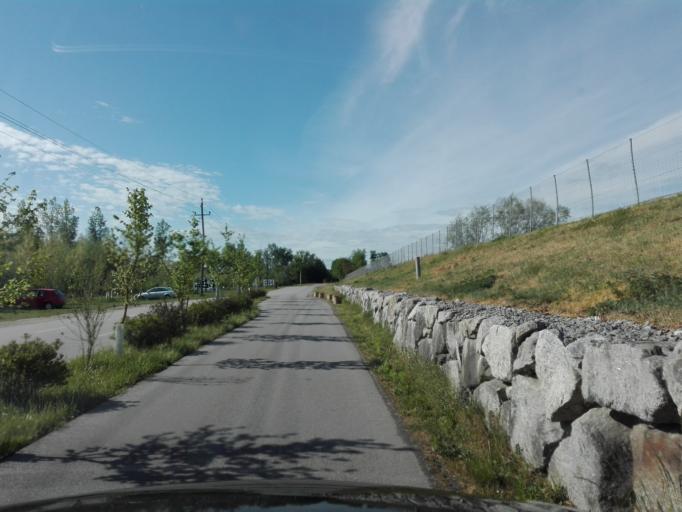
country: AT
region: Upper Austria
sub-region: Politischer Bezirk Linz-Land
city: Asten
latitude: 48.2412
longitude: 14.4165
